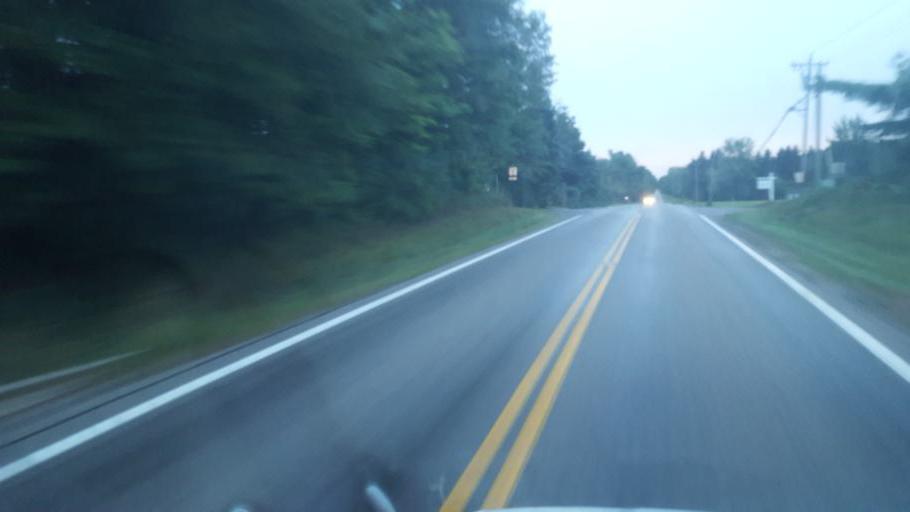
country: US
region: Ohio
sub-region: Knox County
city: Centerburg
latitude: 40.3628
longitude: -82.6900
